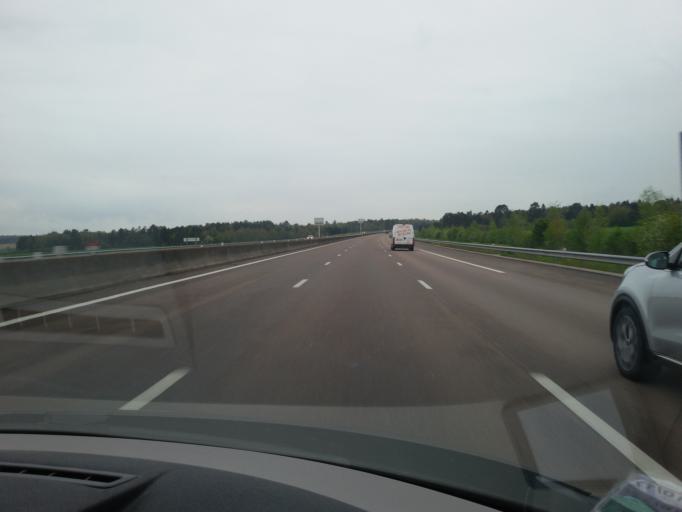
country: FR
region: Bourgogne
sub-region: Departement de la Cote-d'Or
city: Selongey
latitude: 47.5508
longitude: 5.1977
